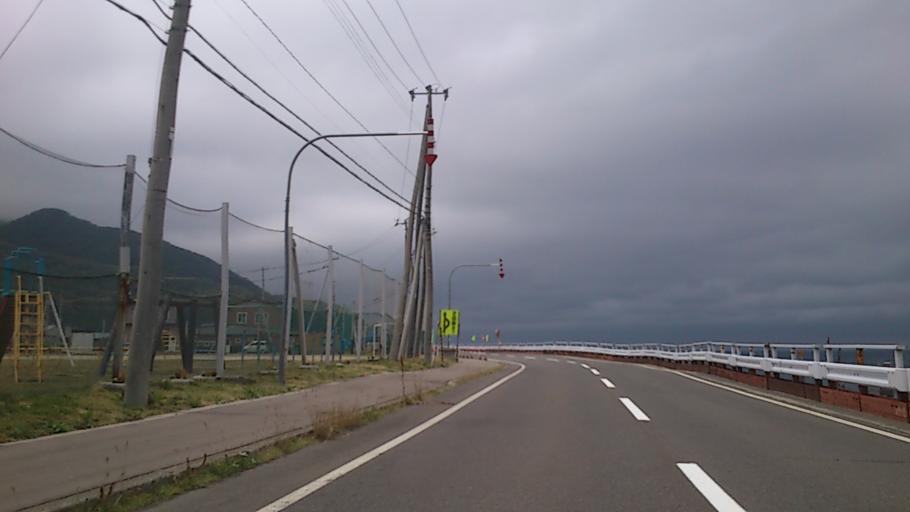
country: JP
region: Hokkaido
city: Iwanai
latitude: 42.6914
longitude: 139.9913
